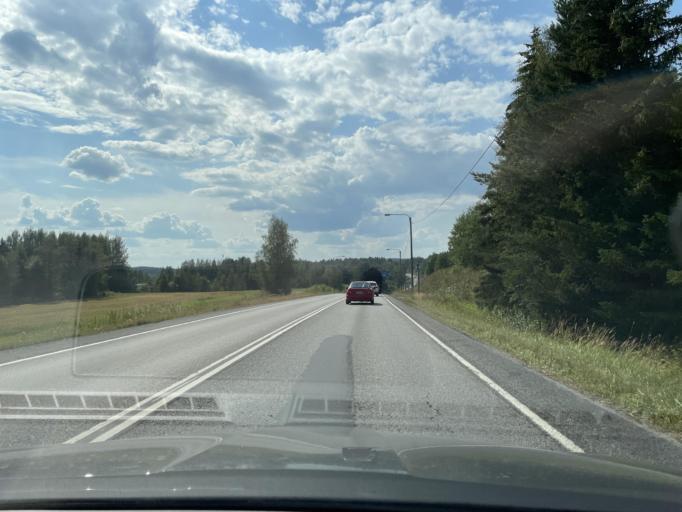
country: FI
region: Central Finland
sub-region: Jyvaeskylae
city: Korpilahti
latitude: 62.0223
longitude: 25.5748
